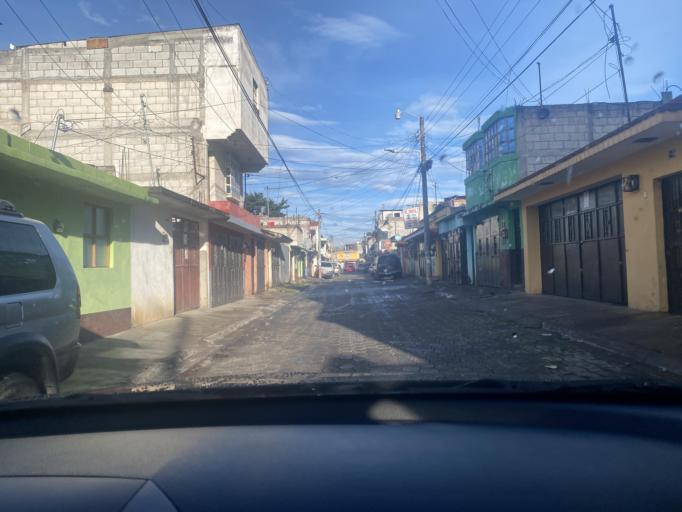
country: GT
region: Quetzaltenango
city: Olintepeque
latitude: 14.8644
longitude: -91.5201
